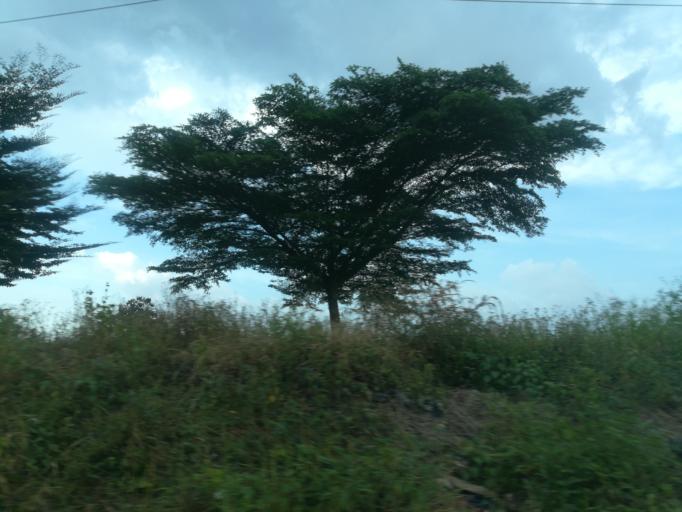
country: NG
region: Oyo
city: Ibadan
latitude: 7.4269
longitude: 3.8827
